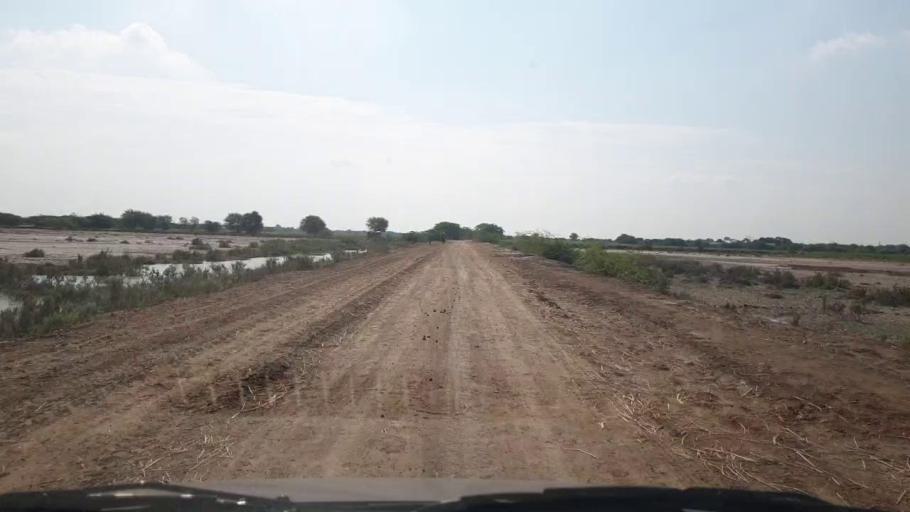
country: PK
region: Sindh
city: Badin
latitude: 24.4880
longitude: 68.6120
